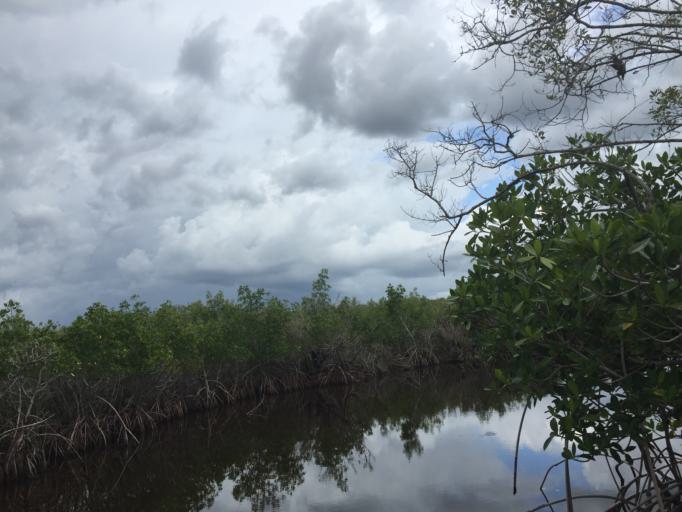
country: US
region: Florida
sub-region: Collier County
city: Marco
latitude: 25.9047
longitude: -81.3718
